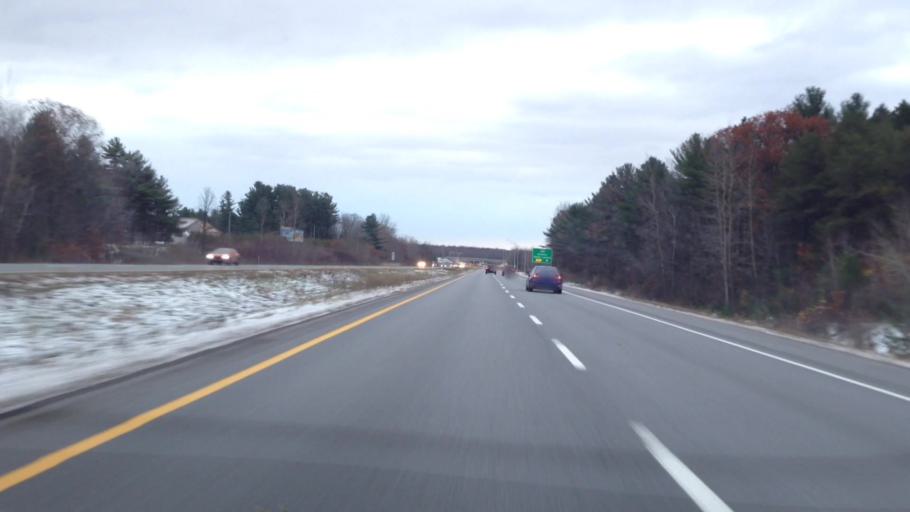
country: CA
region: Quebec
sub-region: Monteregie
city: Hudson
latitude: 45.4312
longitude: -74.1324
